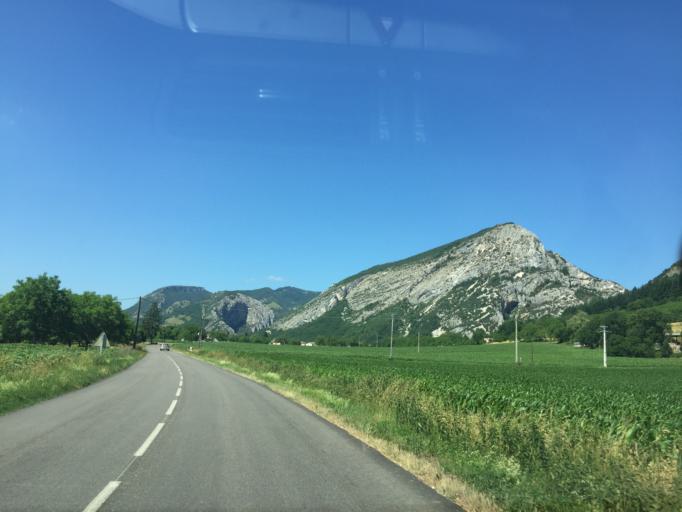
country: FR
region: Rhone-Alpes
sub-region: Departement de la Drome
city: Saint-Laurent-en-Royans
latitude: 45.0393
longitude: 5.3368
